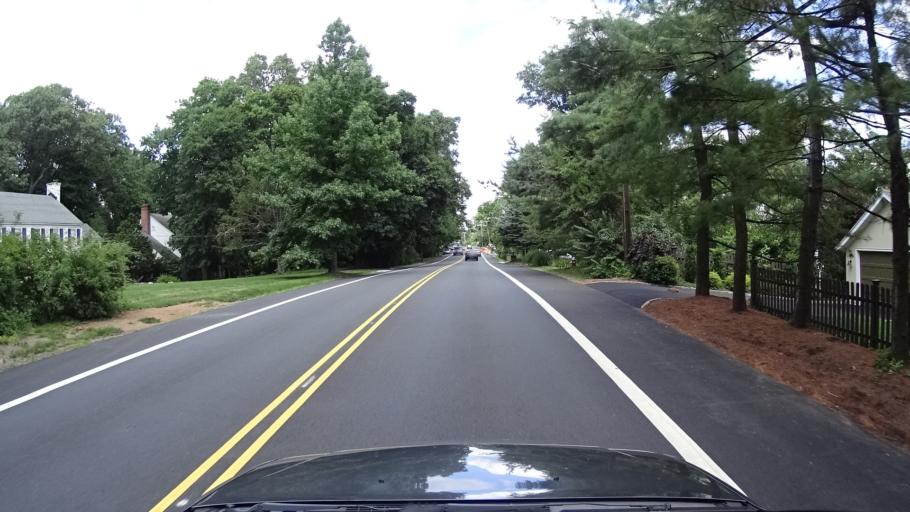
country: US
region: New Jersey
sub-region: Morris County
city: Chatham
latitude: 40.7267
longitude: -74.3956
